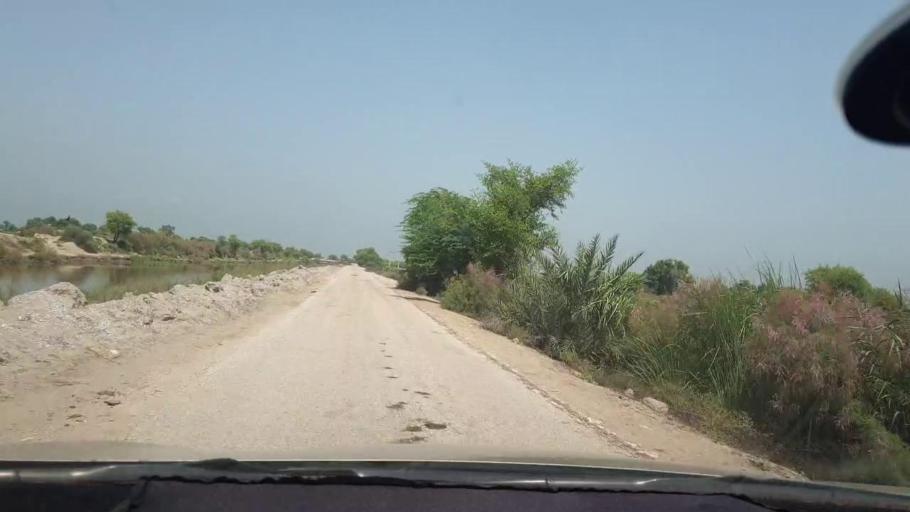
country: PK
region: Sindh
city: Kambar
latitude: 27.6673
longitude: 67.8933
